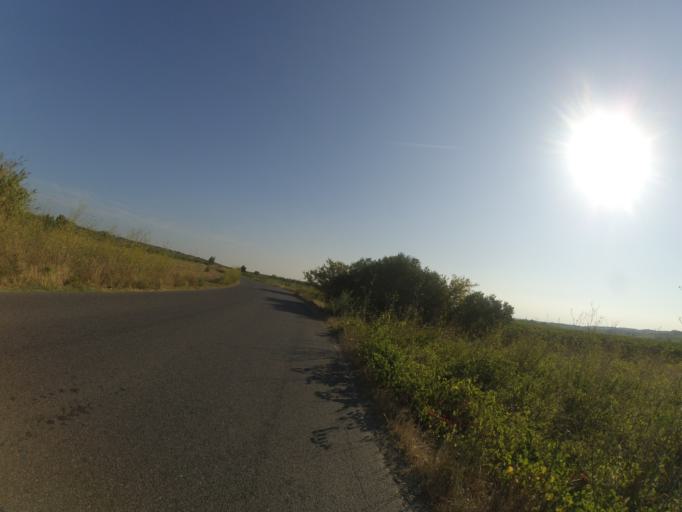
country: FR
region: Languedoc-Roussillon
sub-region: Departement des Pyrenees-Orientales
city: Baixas
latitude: 42.7557
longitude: 2.8172
